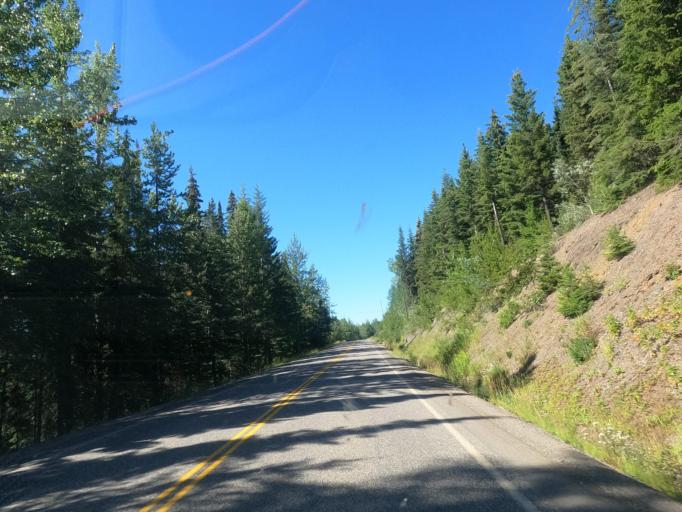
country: CA
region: British Columbia
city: Quesnel
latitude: 53.0303
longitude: -122.0087
